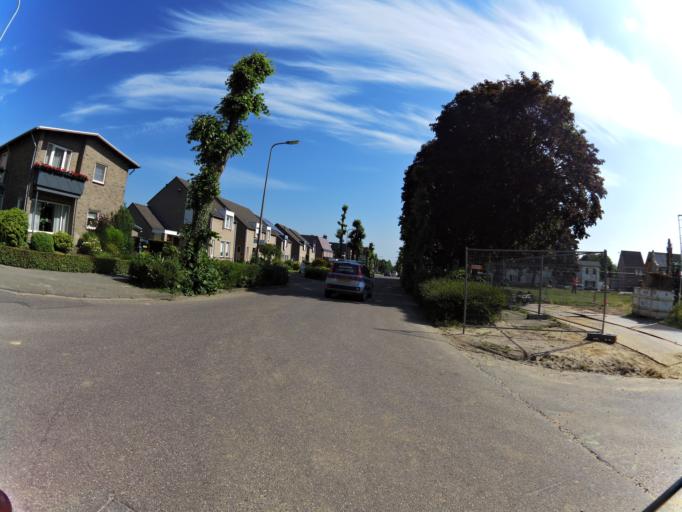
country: NL
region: Limburg
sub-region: Gemeente Kerkrade
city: Kerkrade
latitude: 50.9066
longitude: 6.0338
